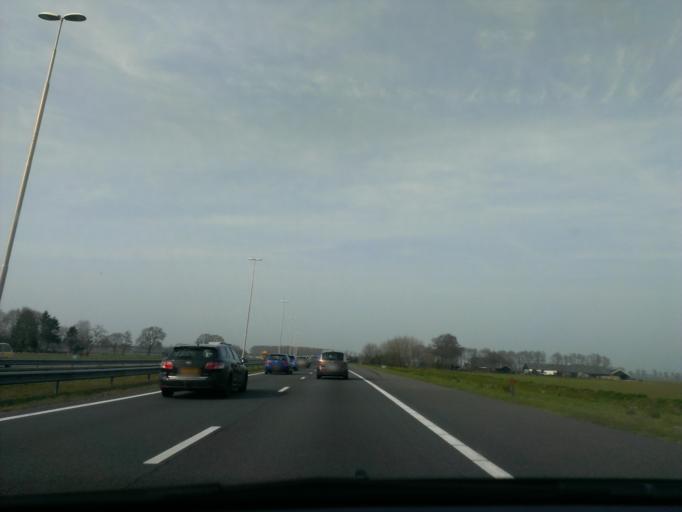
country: NL
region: Gelderland
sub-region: Gemeente Epe
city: Vaassen
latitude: 52.2803
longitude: 6.0085
